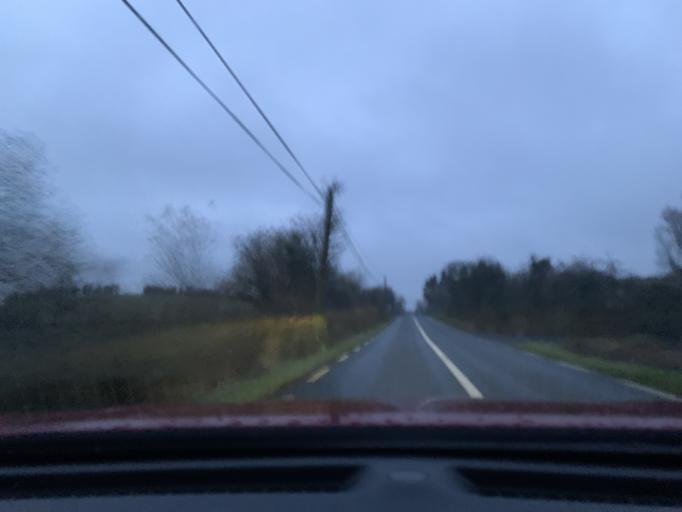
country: IE
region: Connaught
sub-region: Sligo
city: Ballymote
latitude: 54.0369
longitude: -8.5218
